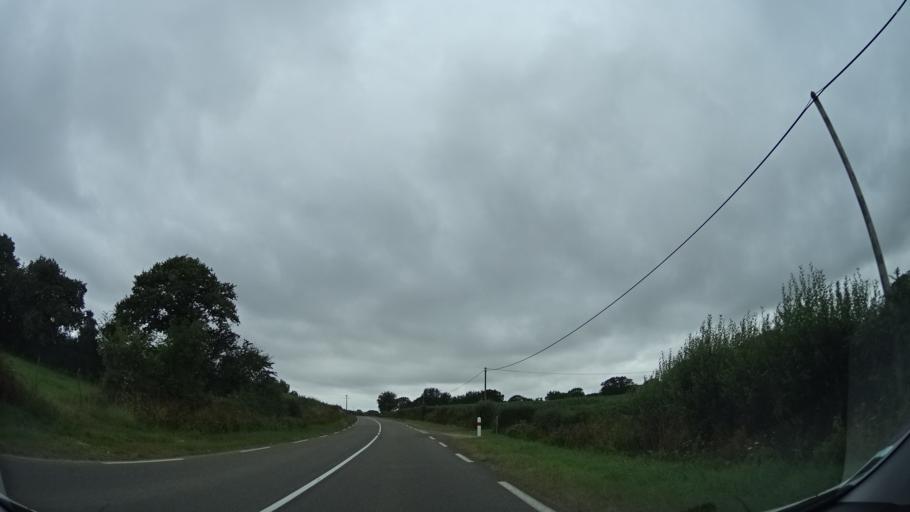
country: FR
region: Lower Normandy
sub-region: Departement de la Manche
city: La Haye-du-Puits
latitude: 49.3105
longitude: -1.6016
